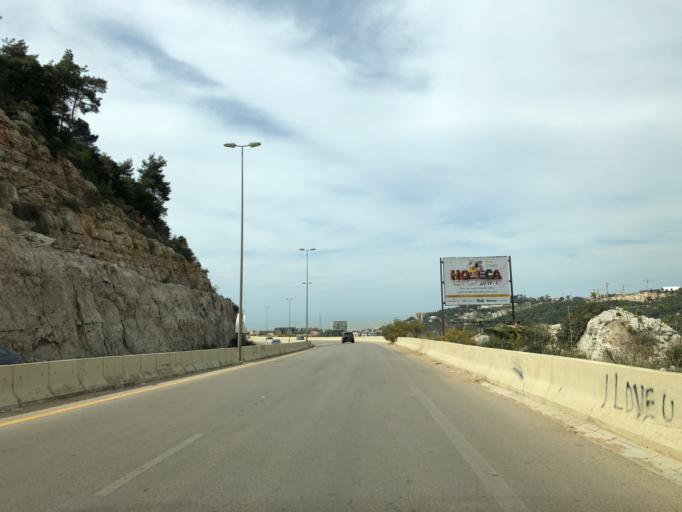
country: LB
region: Mont-Liban
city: Jdaidet el Matn
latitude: 33.8982
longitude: 35.6476
